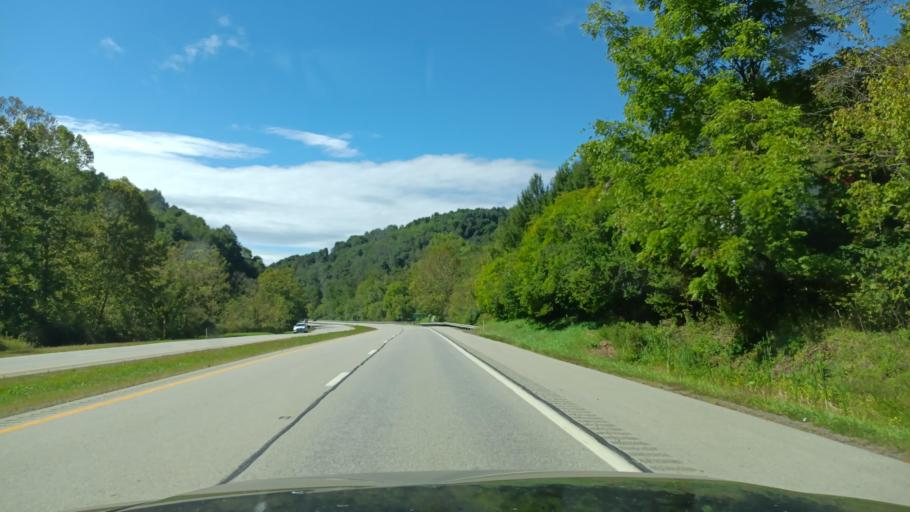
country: US
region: West Virginia
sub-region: Harrison County
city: Salem
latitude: 39.2853
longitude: -80.6522
